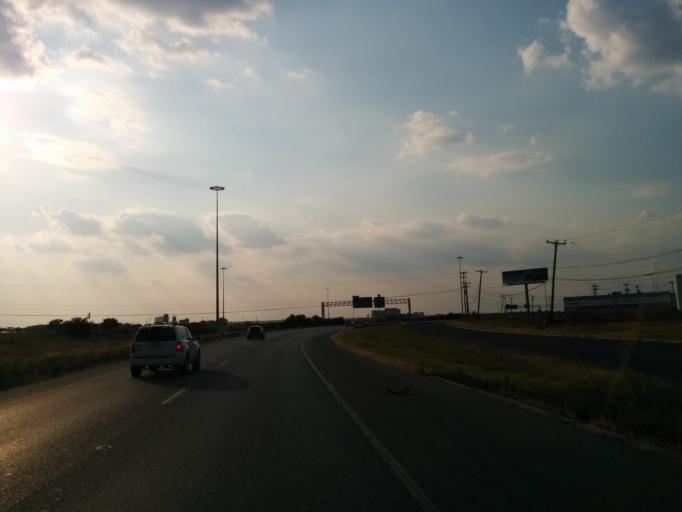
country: US
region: Texas
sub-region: Bexar County
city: Kirby
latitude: 29.4471
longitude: -98.4009
